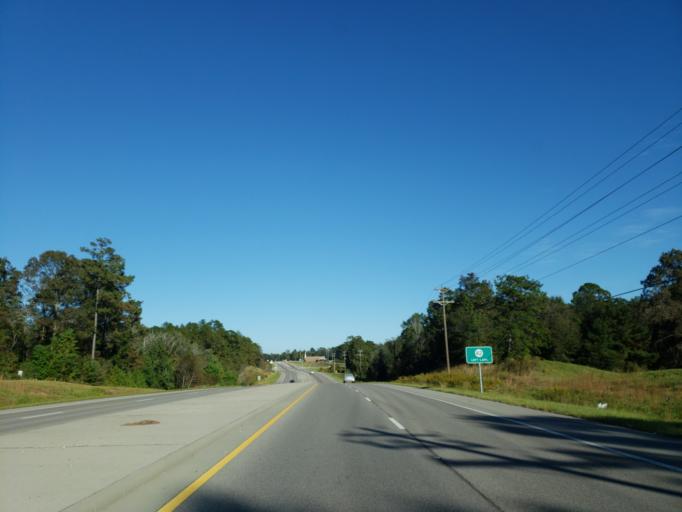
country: US
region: Mississippi
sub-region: Forrest County
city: Petal
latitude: 31.3510
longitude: -89.1814
